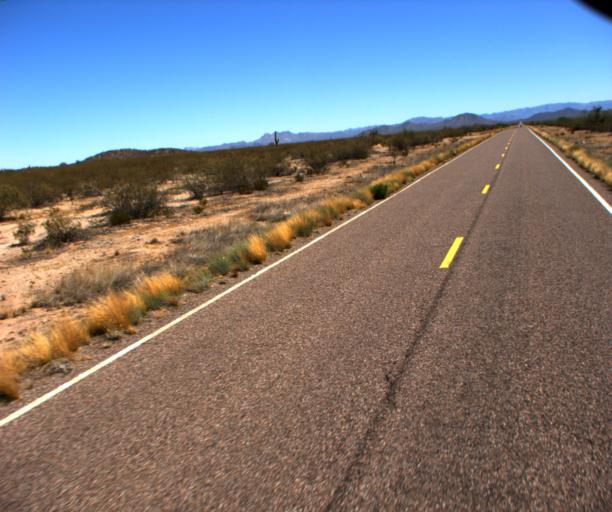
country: US
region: Arizona
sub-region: Yavapai County
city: Congress
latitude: 34.0296
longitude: -113.0846
